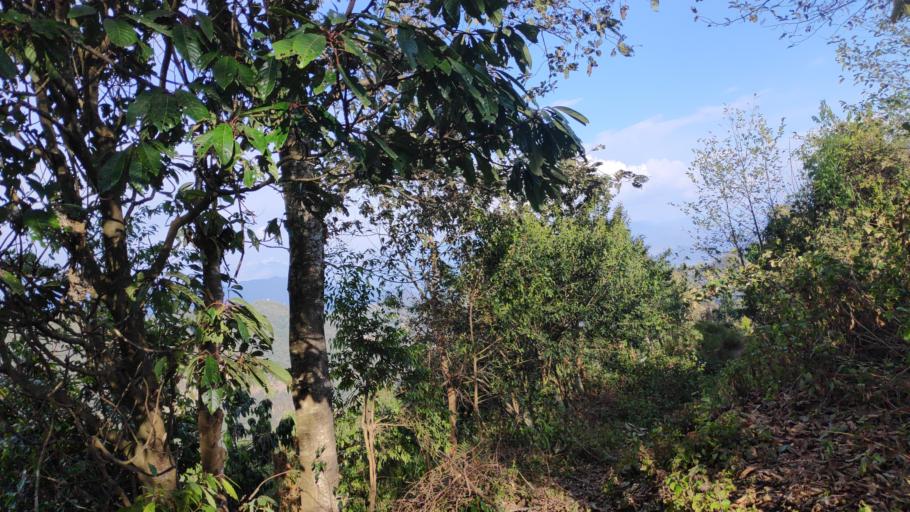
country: NP
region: Western Region
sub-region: Gandaki Zone
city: Pokhara
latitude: 28.2889
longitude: 83.8299
